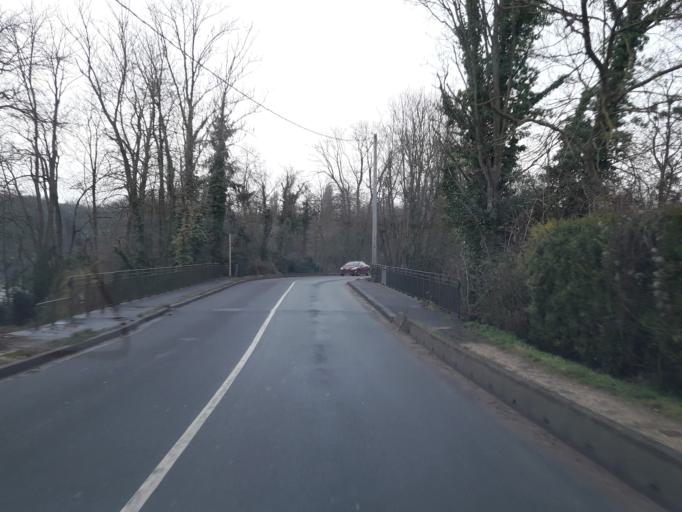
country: FR
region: Ile-de-France
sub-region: Departement de l'Essonne
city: Vert-le-Petit
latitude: 48.5379
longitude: 2.3739
